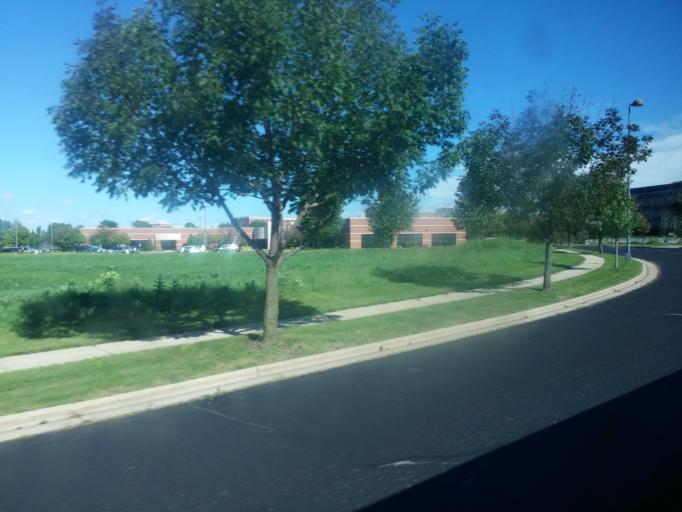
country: US
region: Wisconsin
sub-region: Dane County
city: Maple Bluff
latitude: 43.1428
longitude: -89.2954
